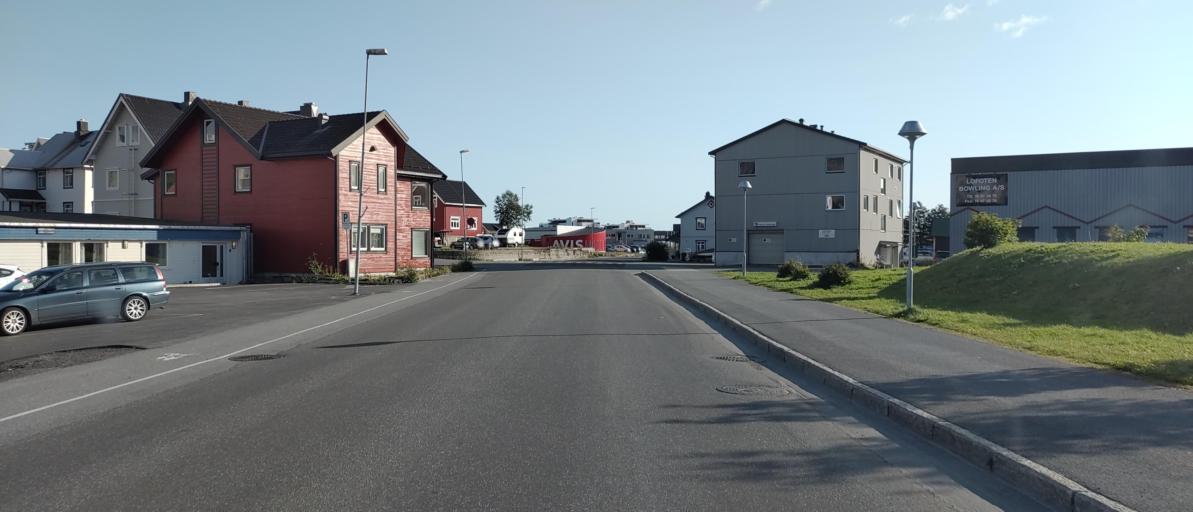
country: NO
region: Nordland
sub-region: Vagan
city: Svolvaer
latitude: 68.2326
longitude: 14.5592
